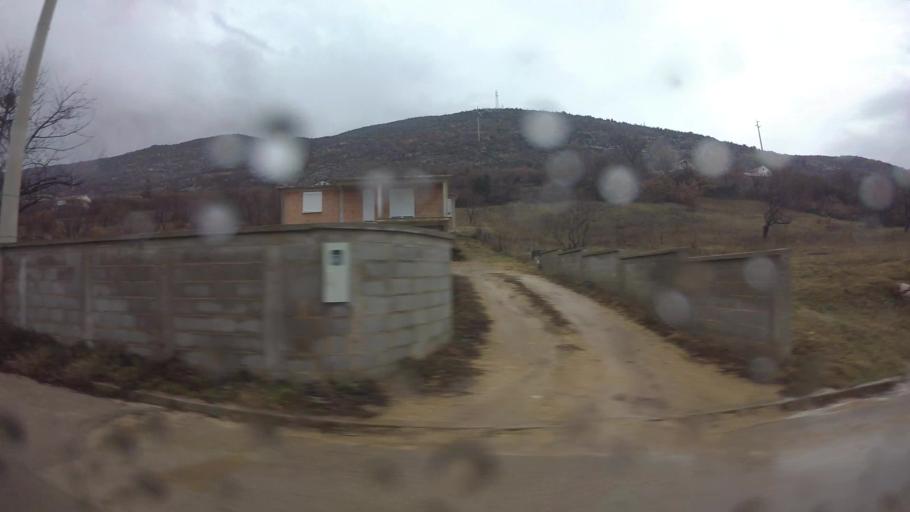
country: BA
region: Federation of Bosnia and Herzegovina
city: Blagaj
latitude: 43.2969
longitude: 17.8561
